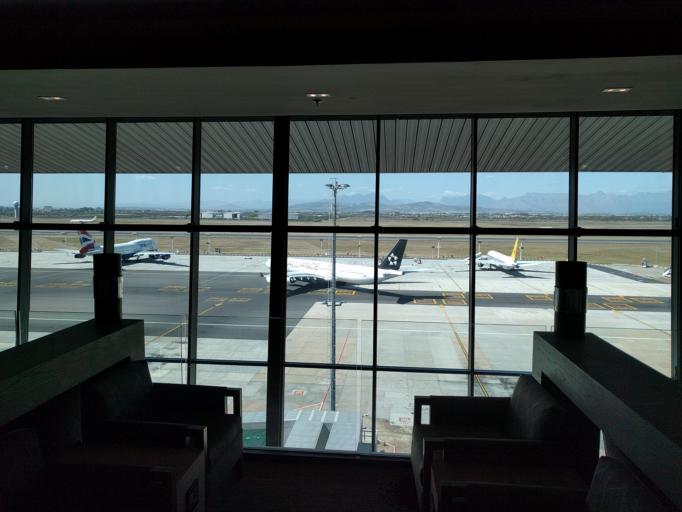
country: ZA
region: Western Cape
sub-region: City of Cape Town
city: Lansdowne
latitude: -33.9694
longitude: 18.5975
